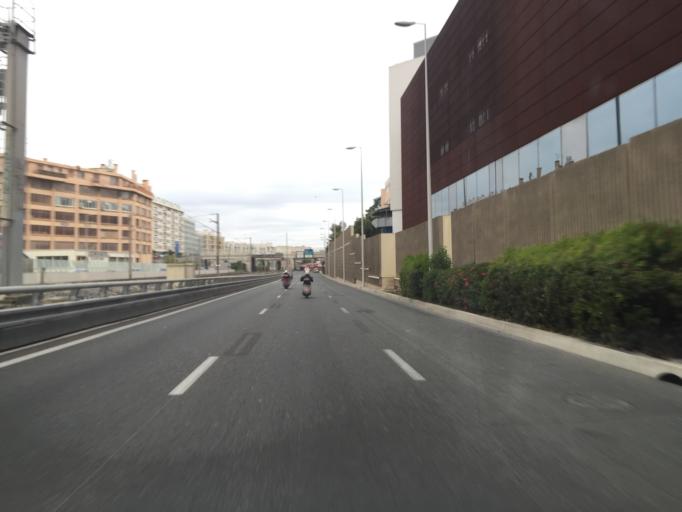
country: FR
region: Provence-Alpes-Cote d'Azur
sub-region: Departement des Alpes-Maritimes
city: Saint-Laurent-du-Var
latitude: 43.6760
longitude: 7.2232
